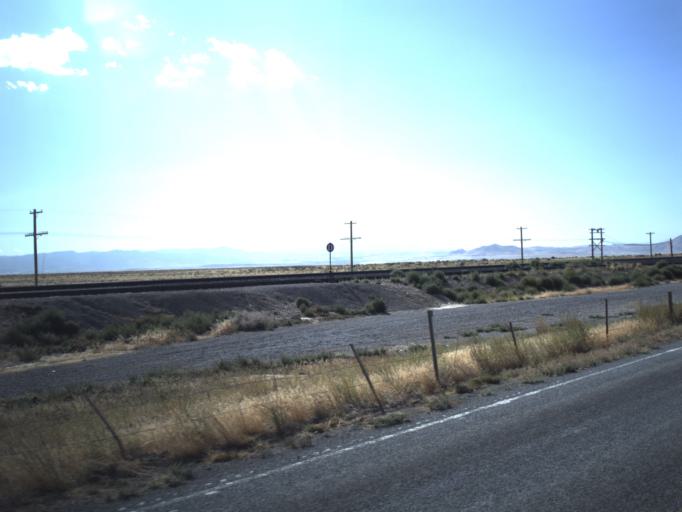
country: US
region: Utah
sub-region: Millard County
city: Delta
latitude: 38.9403
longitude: -112.8081
